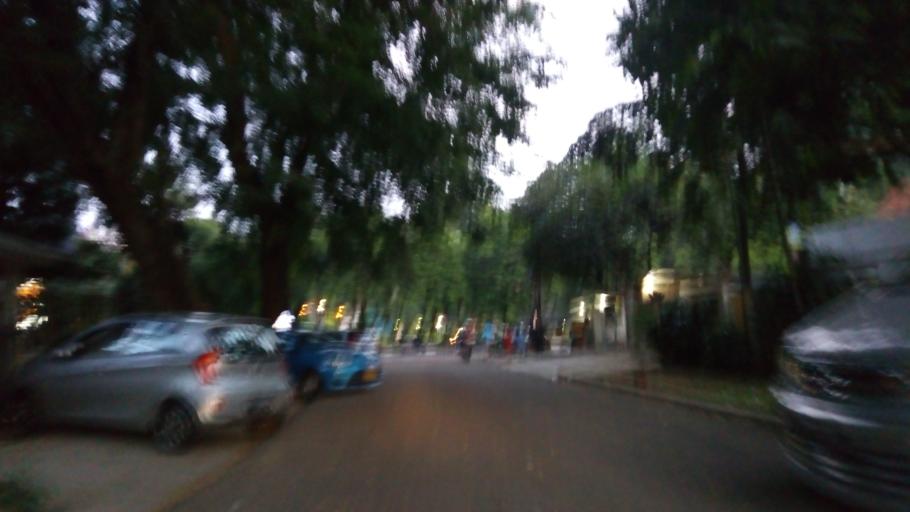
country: ID
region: Jakarta Raya
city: Jakarta
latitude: -6.2444
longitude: 106.7943
